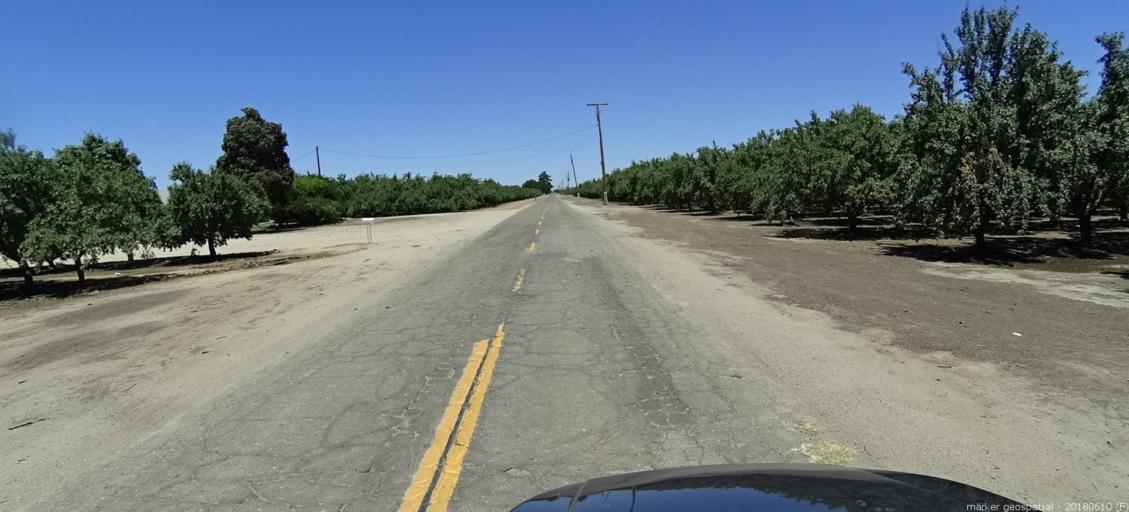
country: US
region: California
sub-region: Madera County
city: Chowchilla
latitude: 37.0695
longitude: -120.2926
